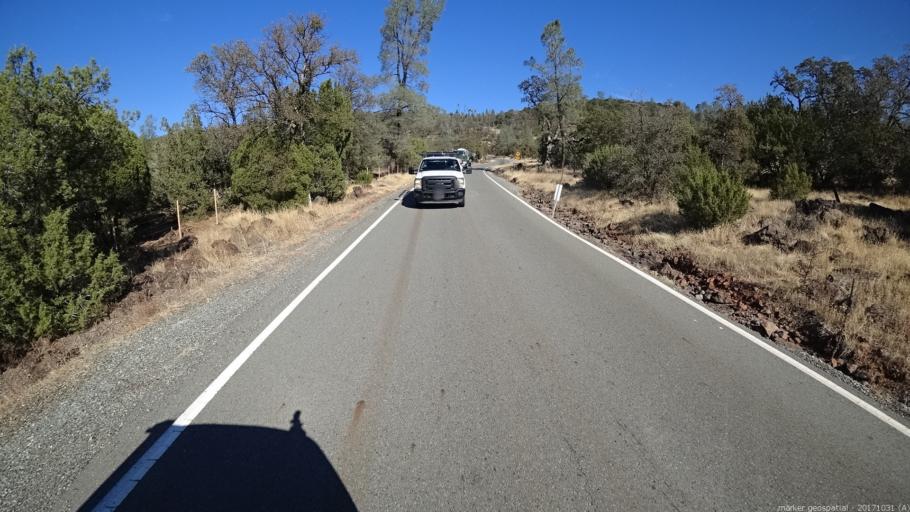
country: US
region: California
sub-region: Shasta County
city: Shingletown
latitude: 40.4561
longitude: -121.8996
